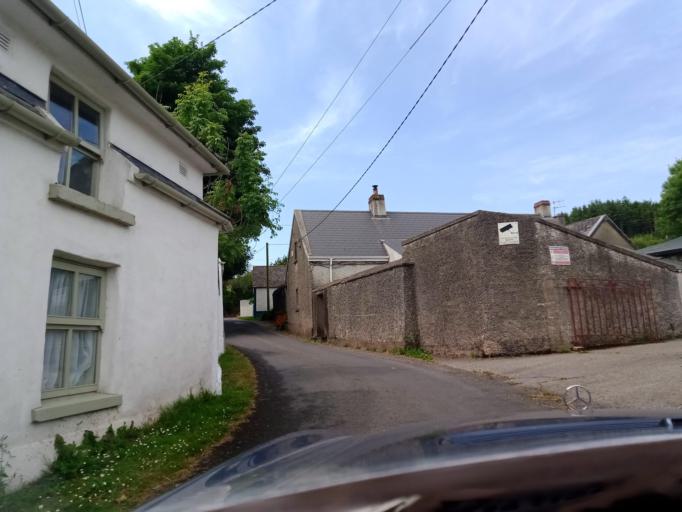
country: IE
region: Leinster
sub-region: Kilkenny
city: Mooncoin
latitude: 52.2551
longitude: -7.2087
